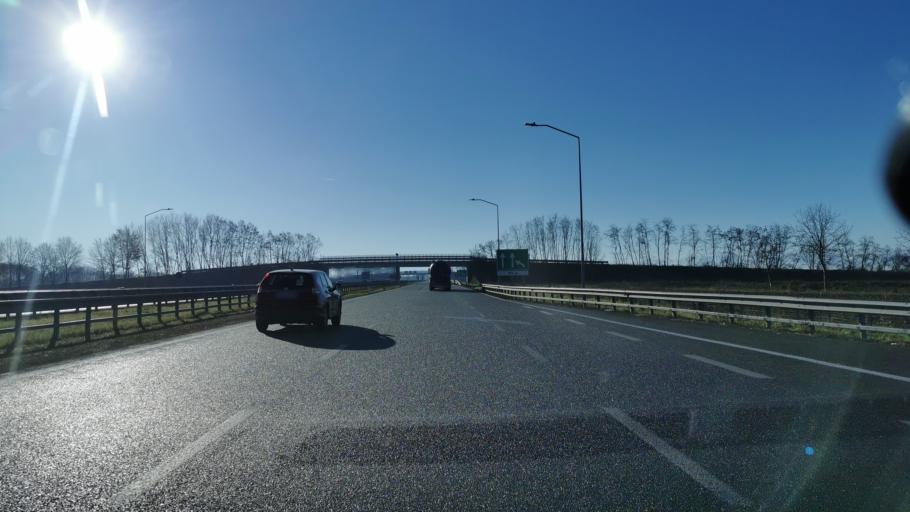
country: IT
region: Piedmont
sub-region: Provincia di Torino
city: Carmagnola
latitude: 44.8497
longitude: 7.7488
